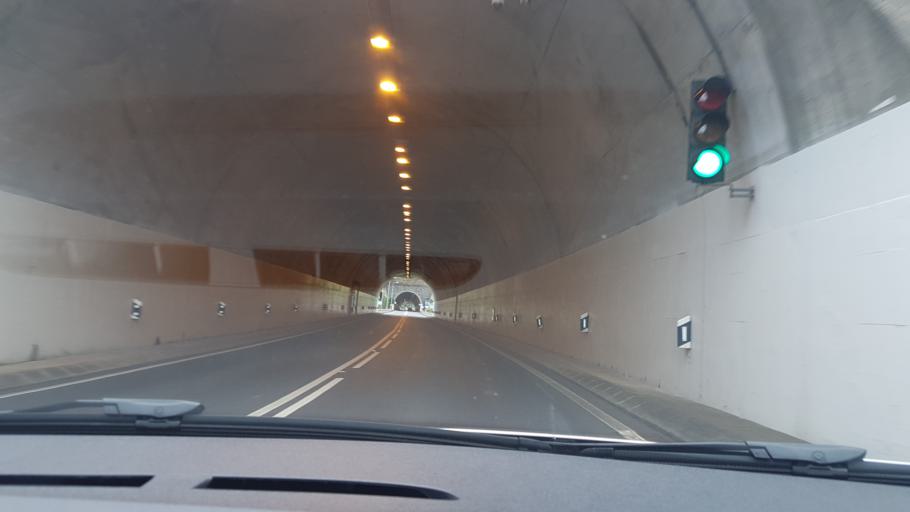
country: PT
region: Madeira
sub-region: Santana
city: Santana
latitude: 32.8096
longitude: -16.8807
